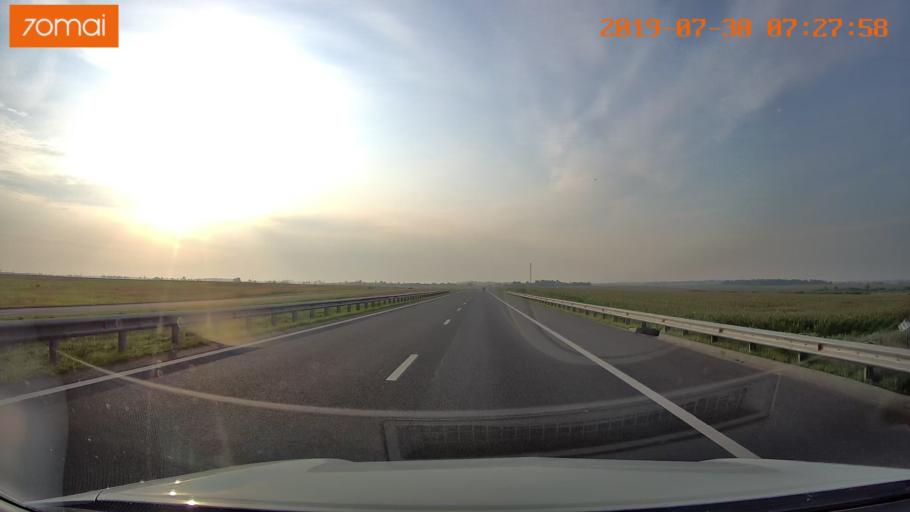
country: RU
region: Kaliningrad
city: Gvardeysk
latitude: 54.6797
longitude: 20.9012
